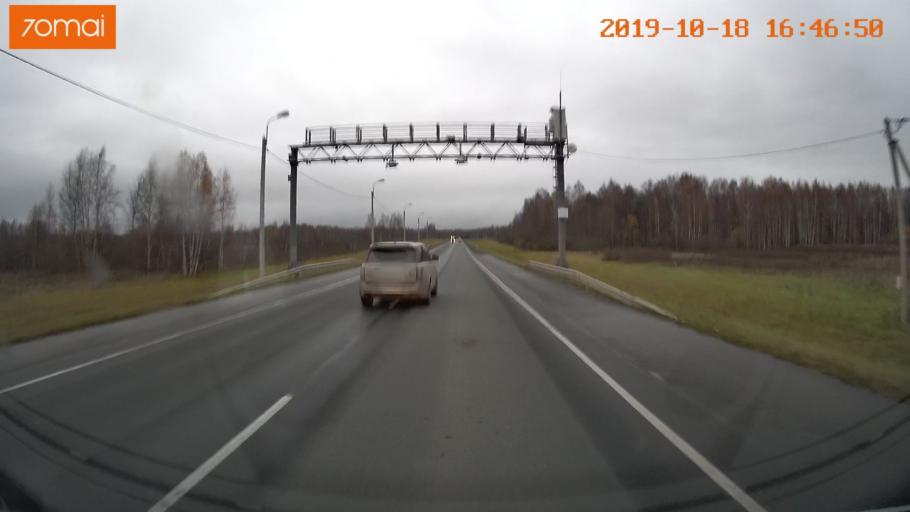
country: RU
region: Vladimir
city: Kideksha
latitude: 56.5215
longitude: 40.5558
